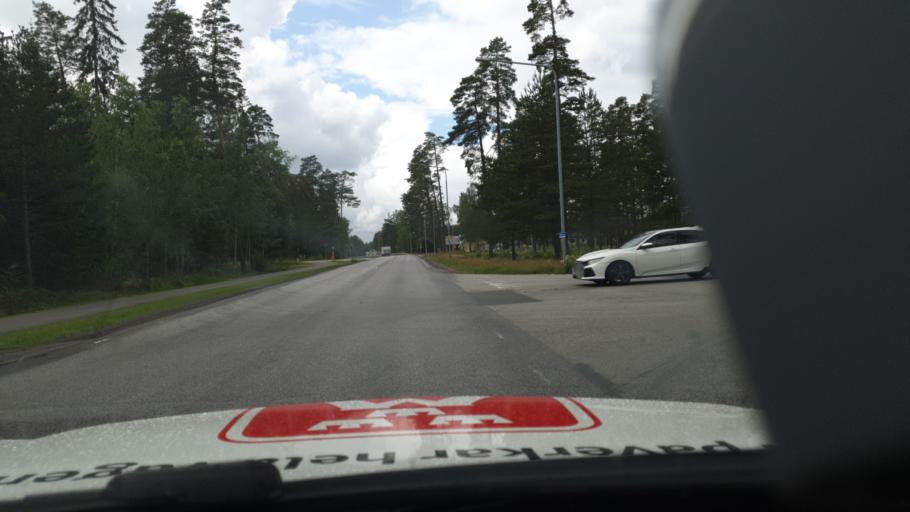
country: SE
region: Joenkoeping
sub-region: Mullsjo Kommun
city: Mullsjoe
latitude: 57.9081
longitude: 13.8693
